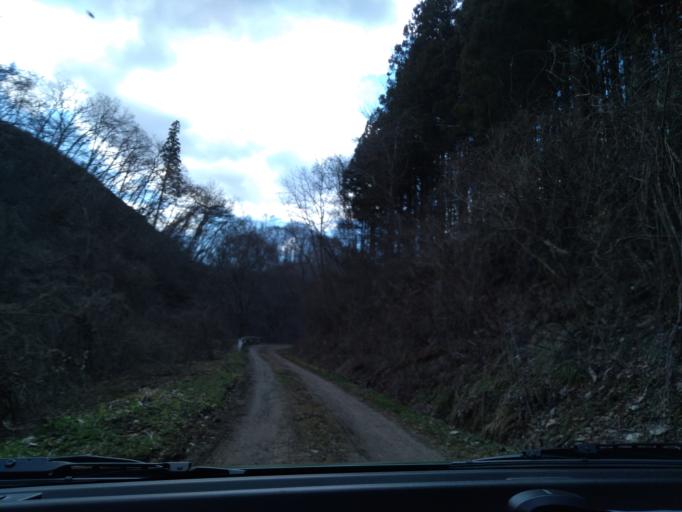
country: JP
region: Iwate
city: Ichinoseki
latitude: 38.9851
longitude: 141.0284
